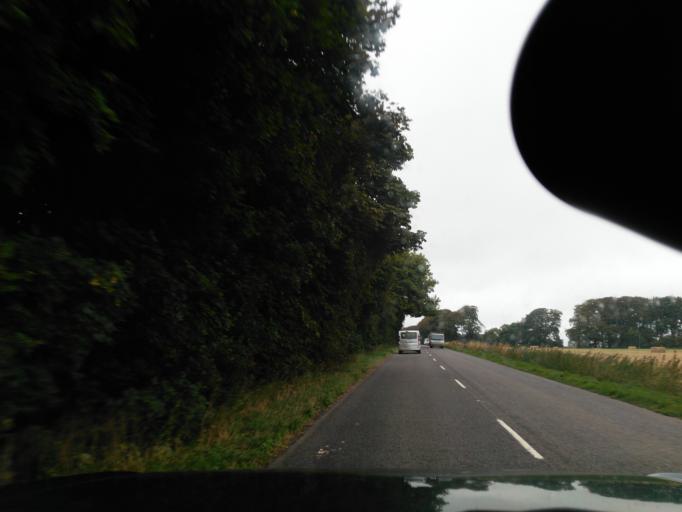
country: GB
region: England
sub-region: Wiltshire
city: Chicklade
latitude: 51.1135
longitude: -2.1693
